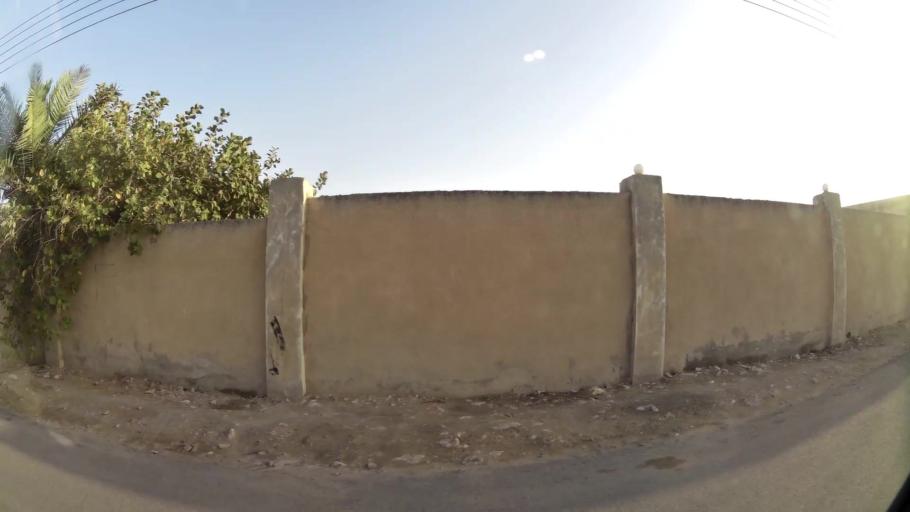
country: QA
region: Baladiyat ar Rayyan
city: Ar Rayyan
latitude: 25.3254
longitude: 51.4576
